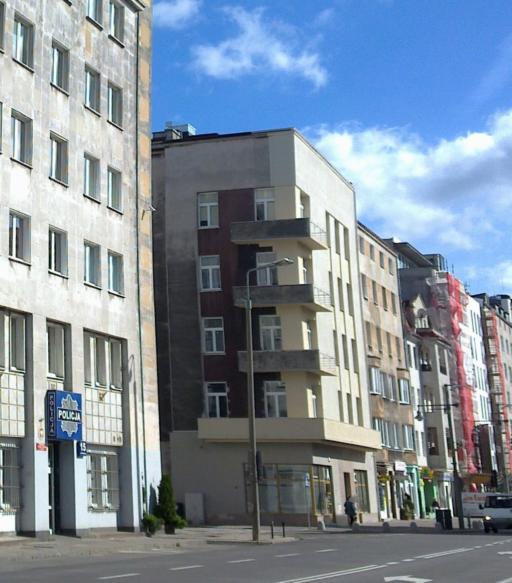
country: PL
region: Pomeranian Voivodeship
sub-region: Gdynia
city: Gdynia
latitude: 54.5244
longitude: 18.5427
